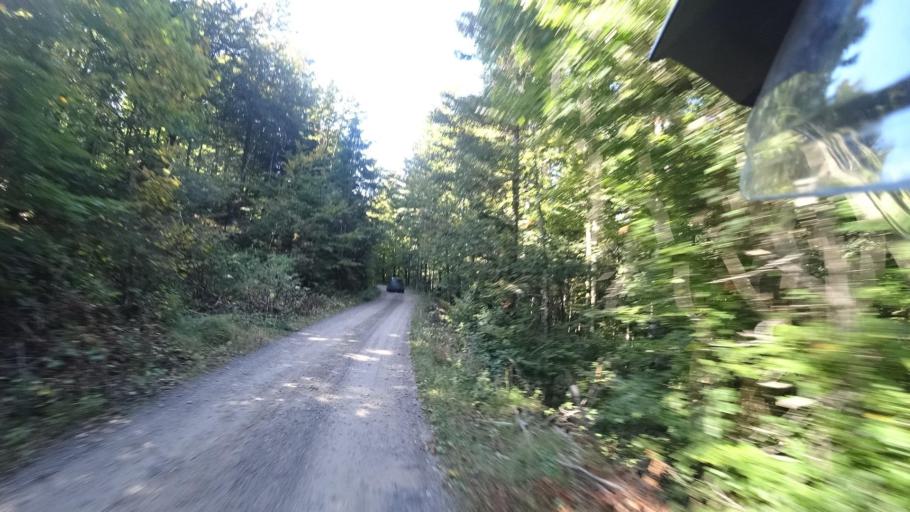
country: HR
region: Karlovacka
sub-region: Grad Ogulin
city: Ogulin
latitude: 45.2290
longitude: 15.1278
